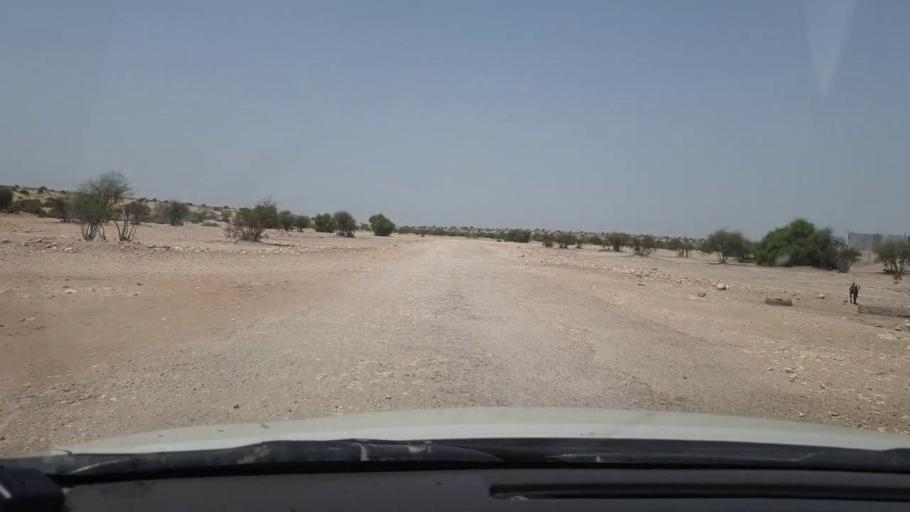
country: PK
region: Sindh
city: Kot Diji
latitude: 27.2847
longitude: 69.2362
